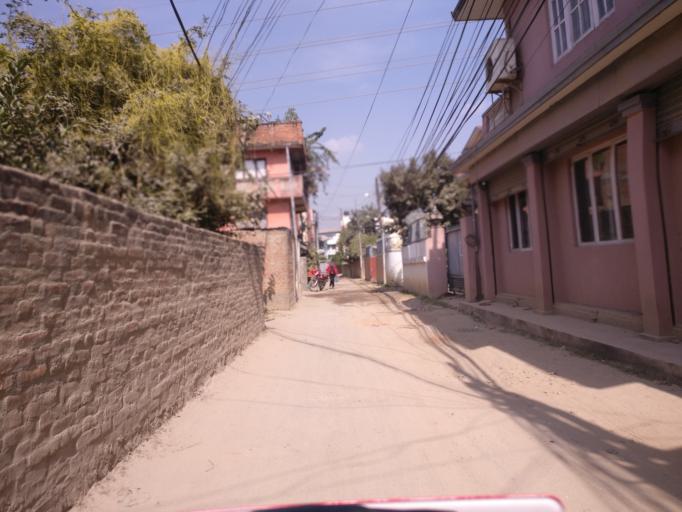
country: NP
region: Central Region
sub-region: Bagmati Zone
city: Patan
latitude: 27.6657
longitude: 85.3157
